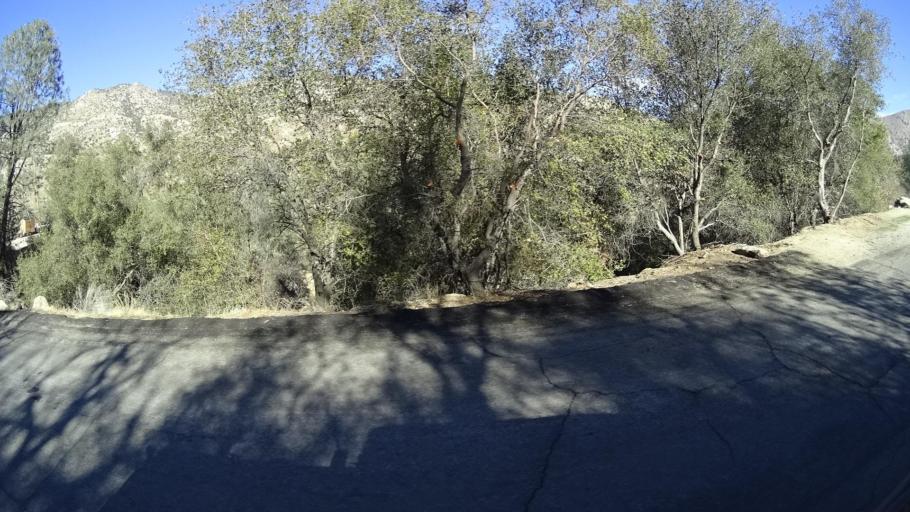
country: US
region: California
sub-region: Kern County
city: Bodfish
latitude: 35.5751
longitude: -118.5518
